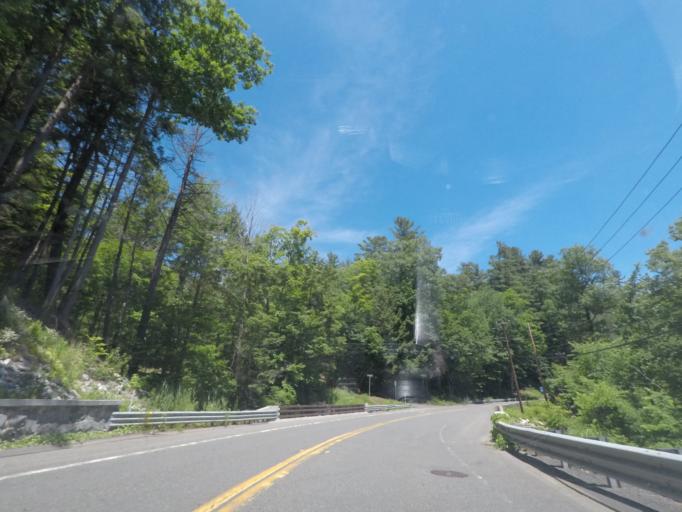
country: US
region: Massachusetts
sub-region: Berkshire County
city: Becket
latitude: 42.2738
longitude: -72.9998
